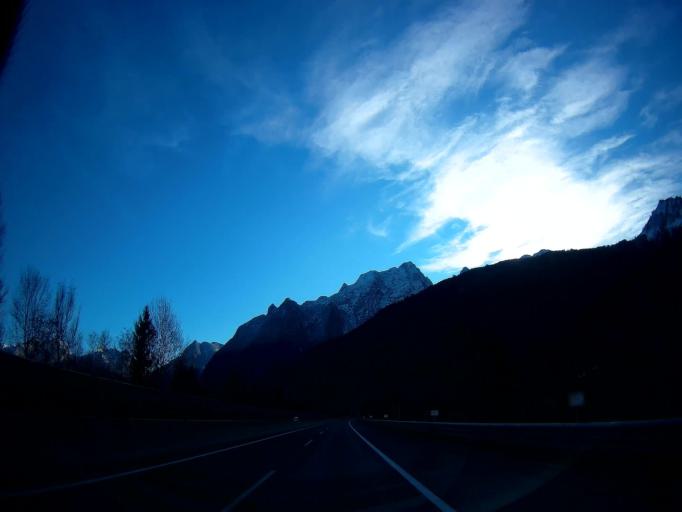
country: AT
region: Salzburg
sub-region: Politischer Bezirk Hallein
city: Kuchl
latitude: 47.6388
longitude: 13.1346
